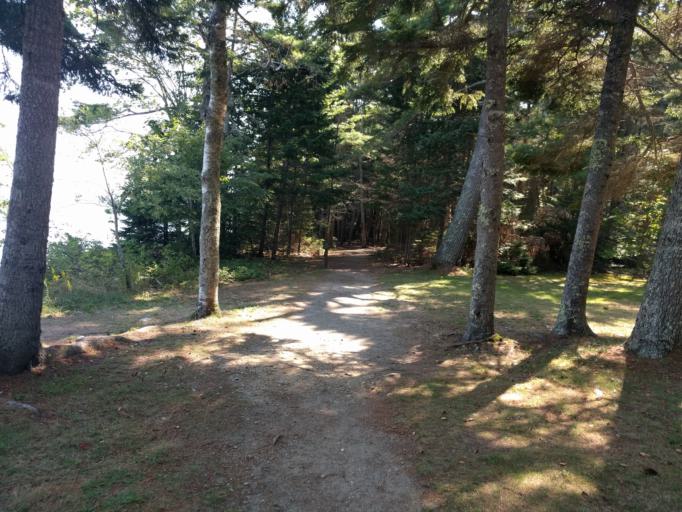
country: US
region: Maine
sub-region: Waldo County
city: Belfast
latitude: 44.4302
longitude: -68.9431
